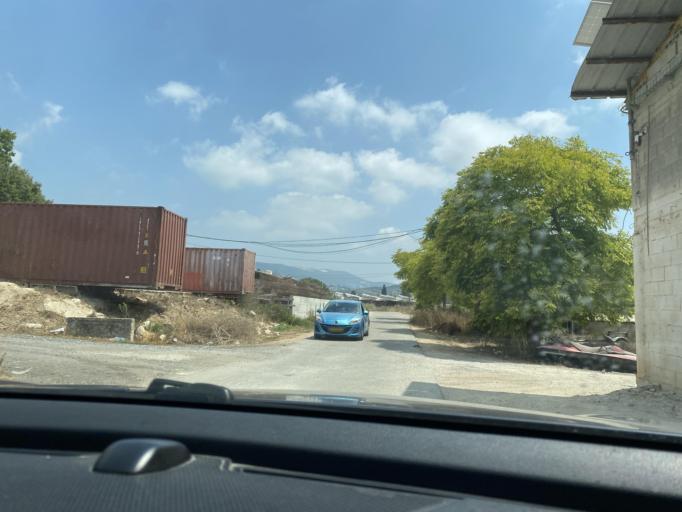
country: IL
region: Northern District
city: Kefar Weradim
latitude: 32.9981
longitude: 35.2988
